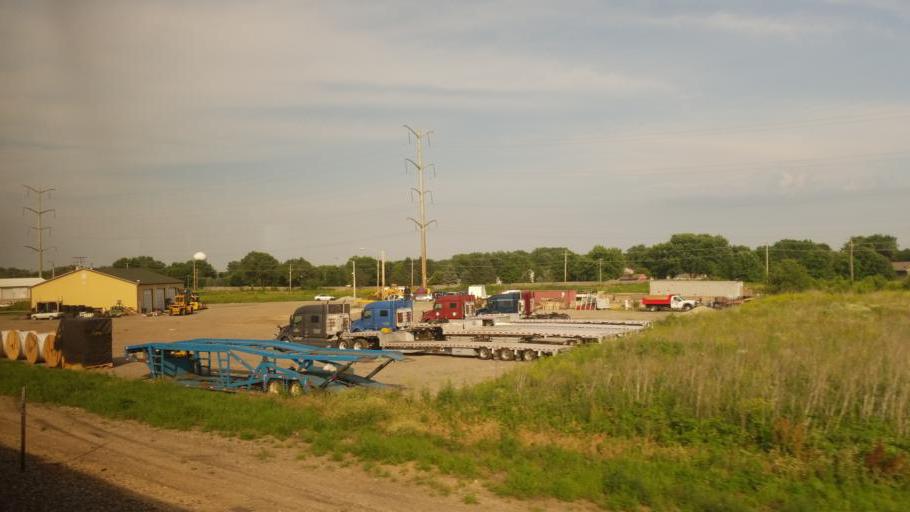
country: US
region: Illinois
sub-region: Kendall County
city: Oswego
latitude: 41.7025
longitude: -88.3694
